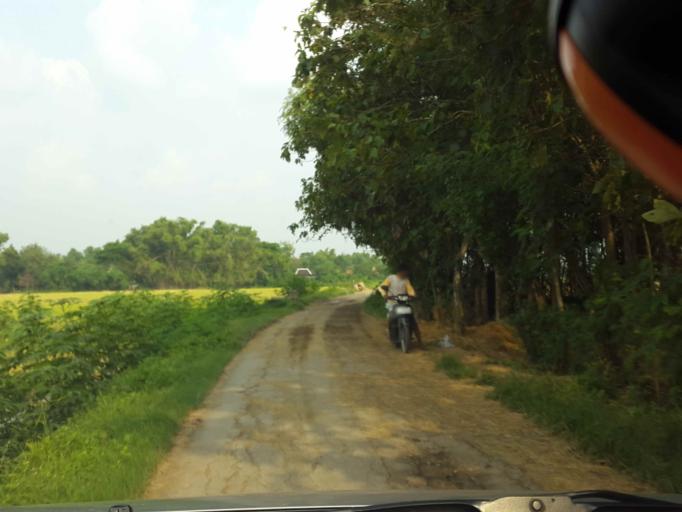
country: ID
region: Central Java
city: Sragen
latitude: -7.4034
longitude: 110.8975
